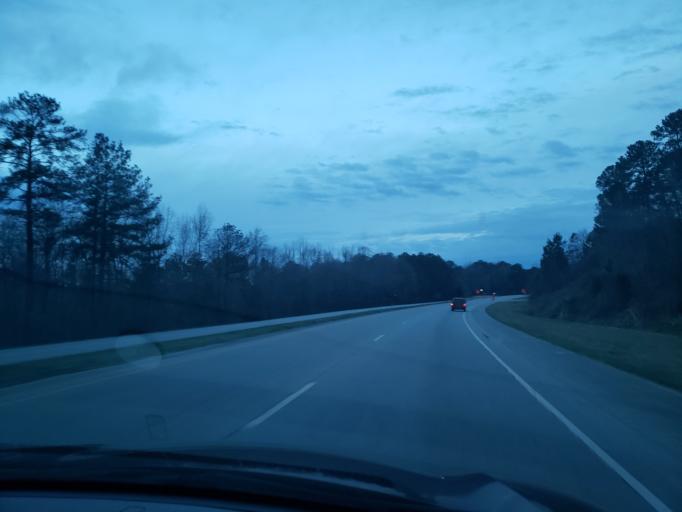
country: US
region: Alabama
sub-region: Lee County
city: Auburn
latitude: 32.6587
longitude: -85.4640
